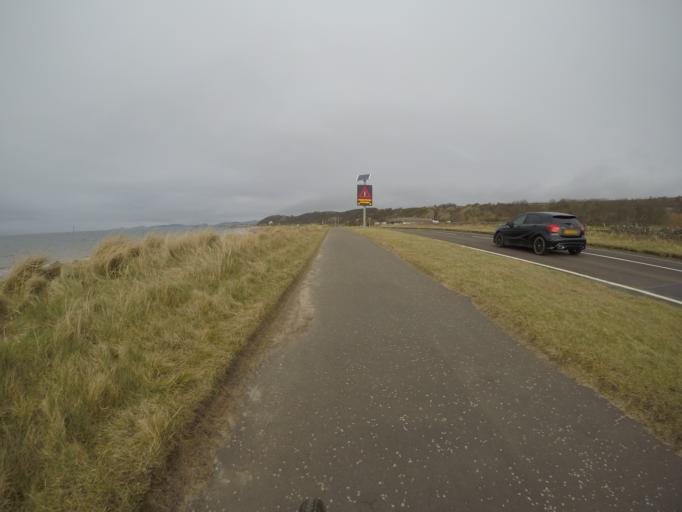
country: GB
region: Scotland
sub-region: North Ayrshire
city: Ardrossan
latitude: 55.6597
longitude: -4.8308
